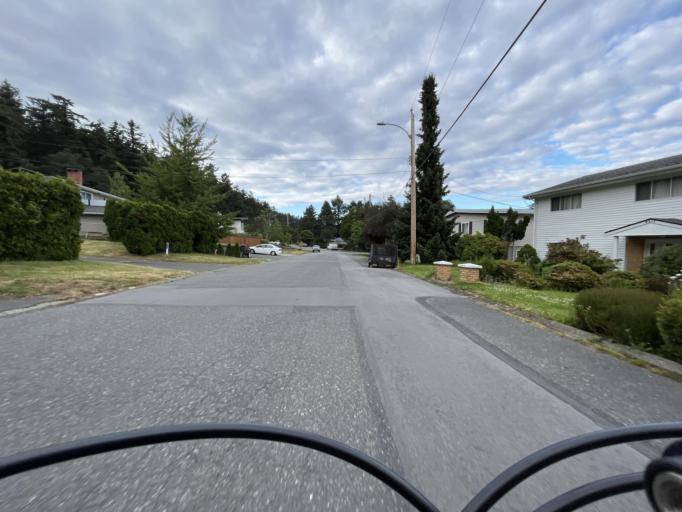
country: CA
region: British Columbia
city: Oak Bay
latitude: 48.4824
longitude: -123.3439
